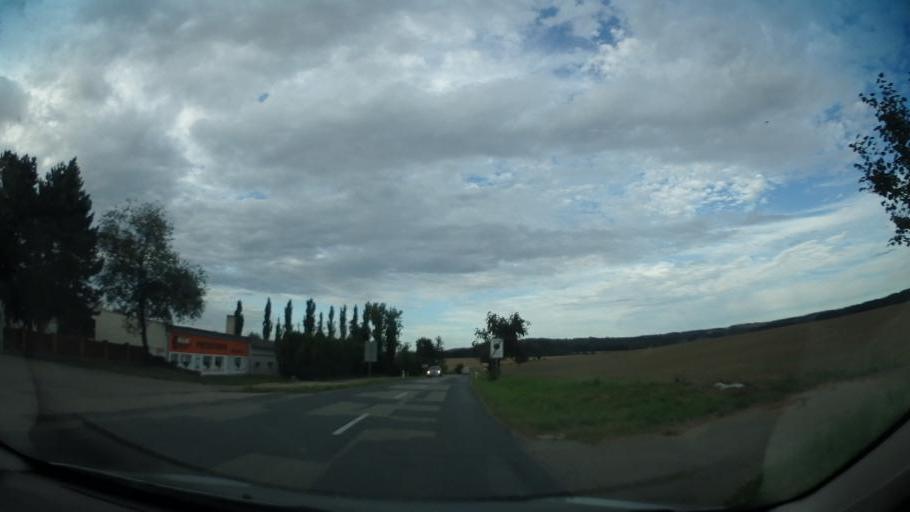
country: CZ
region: South Moravian
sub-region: Okres Blansko
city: Boskovice
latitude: 49.4988
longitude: 16.6656
